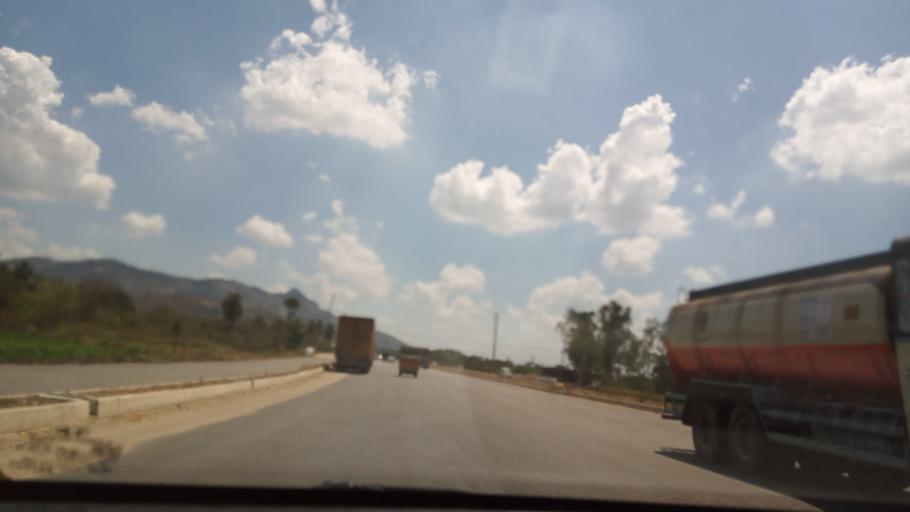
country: IN
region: Andhra Pradesh
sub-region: Chittoor
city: Pakala
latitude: 13.3501
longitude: 79.0840
